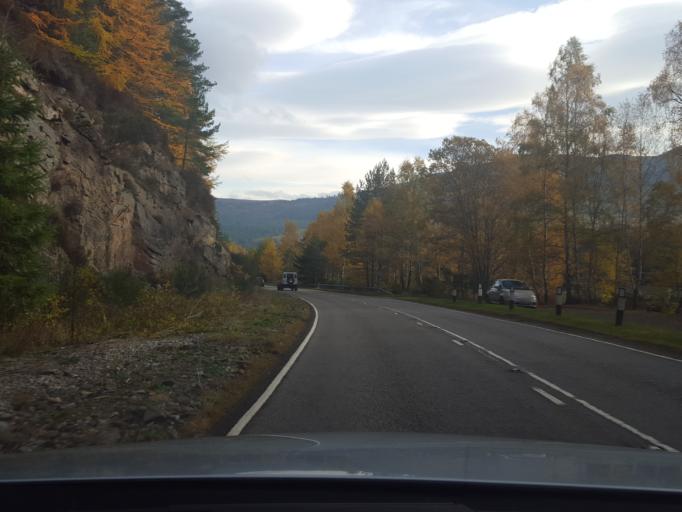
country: GB
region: Scotland
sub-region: Highland
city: Spean Bridge
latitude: 57.2028
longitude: -4.7233
